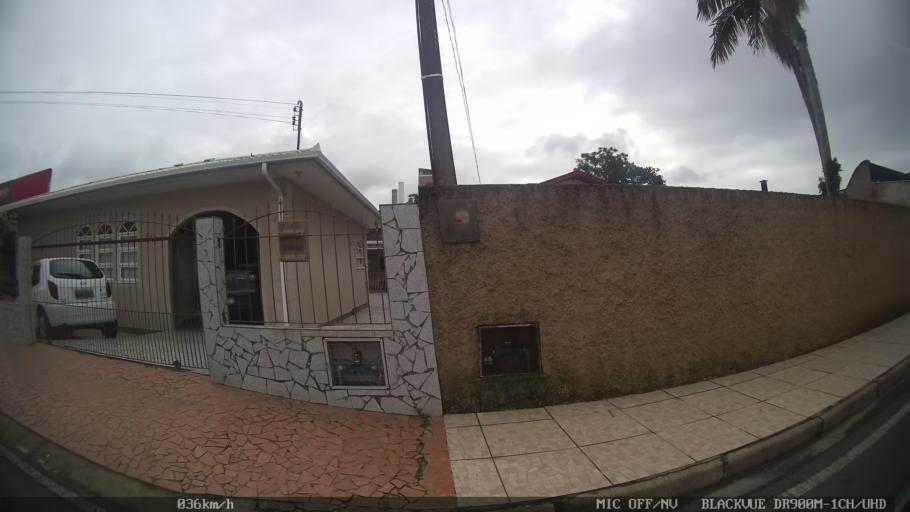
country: BR
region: Santa Catarina
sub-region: Biguacu
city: Biguacu
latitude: -27.5363
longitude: -48.6366
